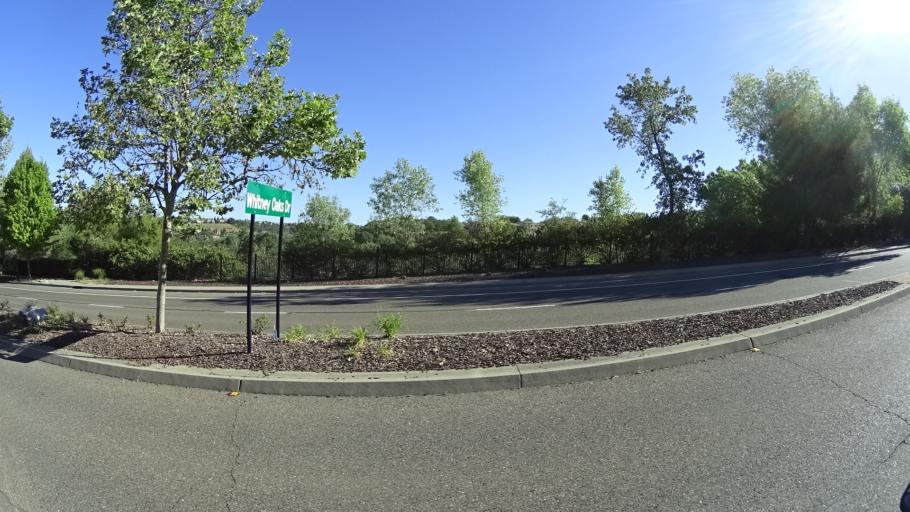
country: US
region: California
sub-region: Placer County
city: Rocklin
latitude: 38.8205
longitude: -121.2422
